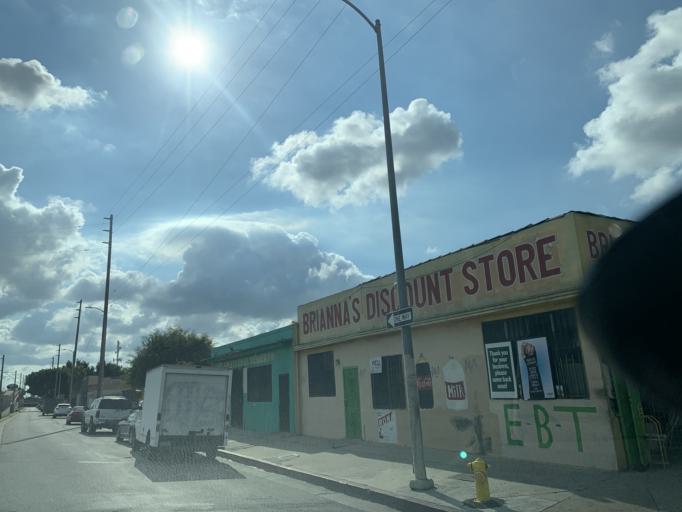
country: US
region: California
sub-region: Los Angeles County
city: Huntington Park
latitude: 33.9930
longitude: -118.2435
